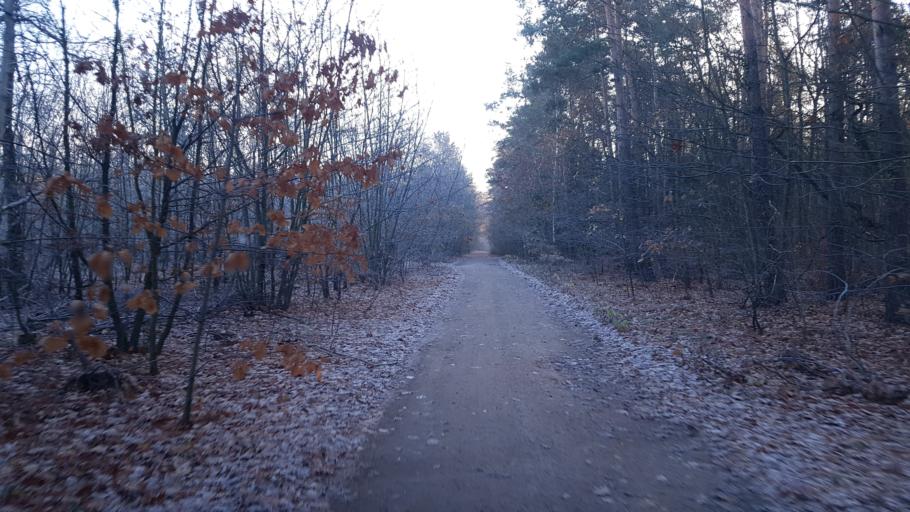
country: DE
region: Brandenburg
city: Sallgast
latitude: 51.5899
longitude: 13.8384
